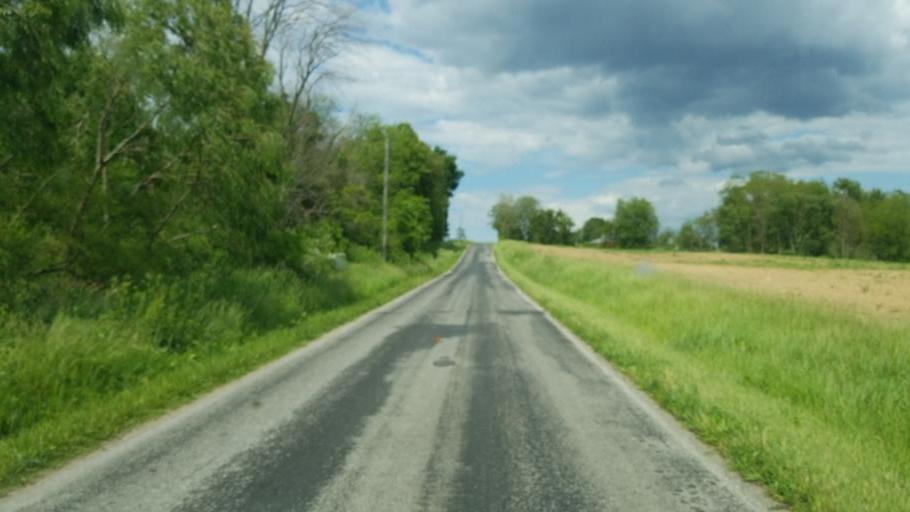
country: US
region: Ohio
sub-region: Huron County
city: Greenwich
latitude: 40.9326
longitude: -82.5502
